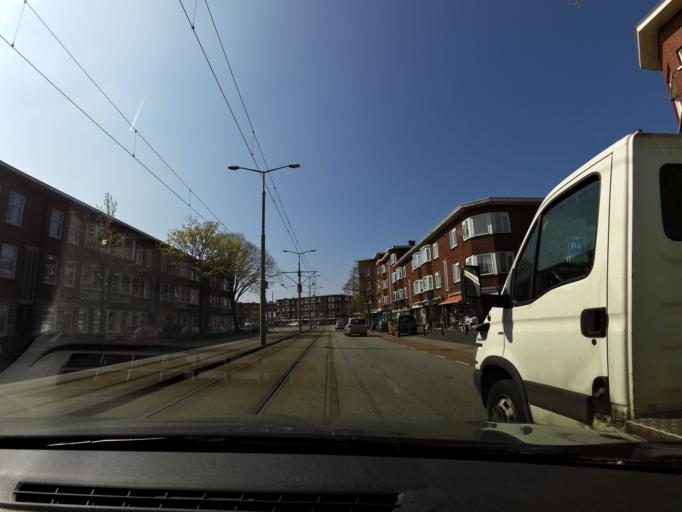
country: NL
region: South Holland
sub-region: Gemeente Rijswijk
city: Rijswijk
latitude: 52.0605
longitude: 4.3297
